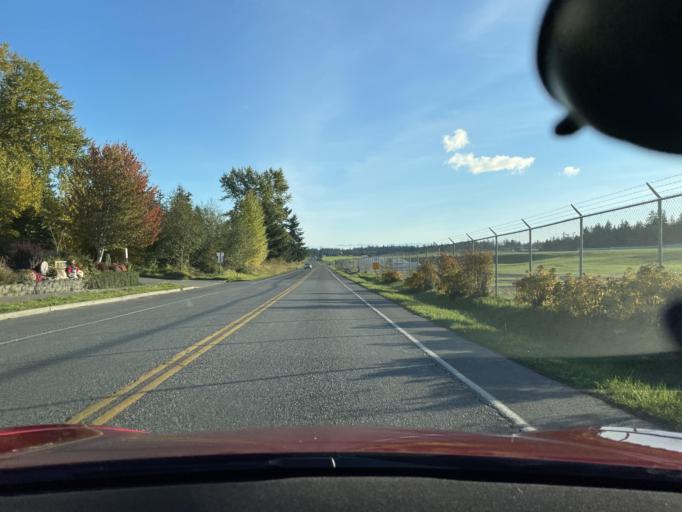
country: US
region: Washington
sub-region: San Juan County
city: Friday Harbor
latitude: 48.5258
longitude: -123.0232
